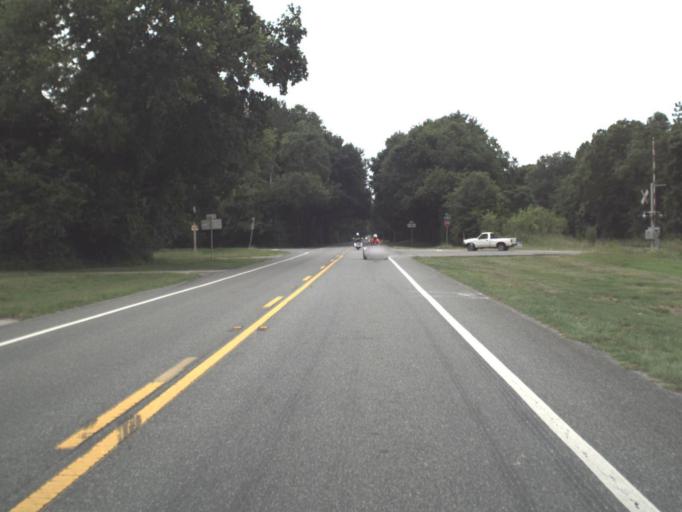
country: US
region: Florida
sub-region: Alachua County
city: Newberry
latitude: 29.6110
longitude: -82.5874
